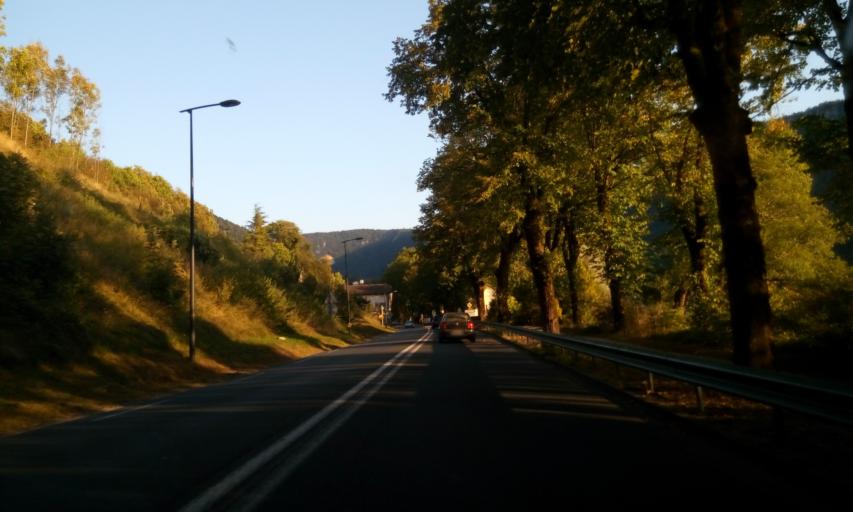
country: FR
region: Rhone-Alpes
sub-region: Departement de l'Ain
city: Nantua
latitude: 46.1604
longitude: 5.6010
